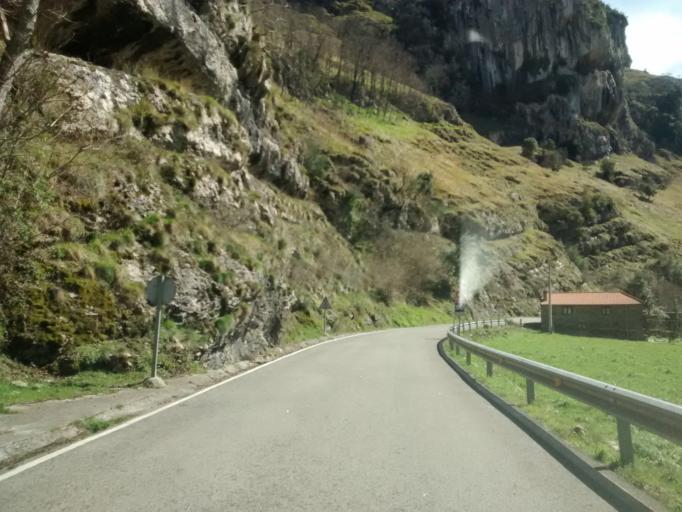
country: ES
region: Cantabria
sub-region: Provincia de Cantabria
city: Selaya
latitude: 43.2489
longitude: -3.7088
